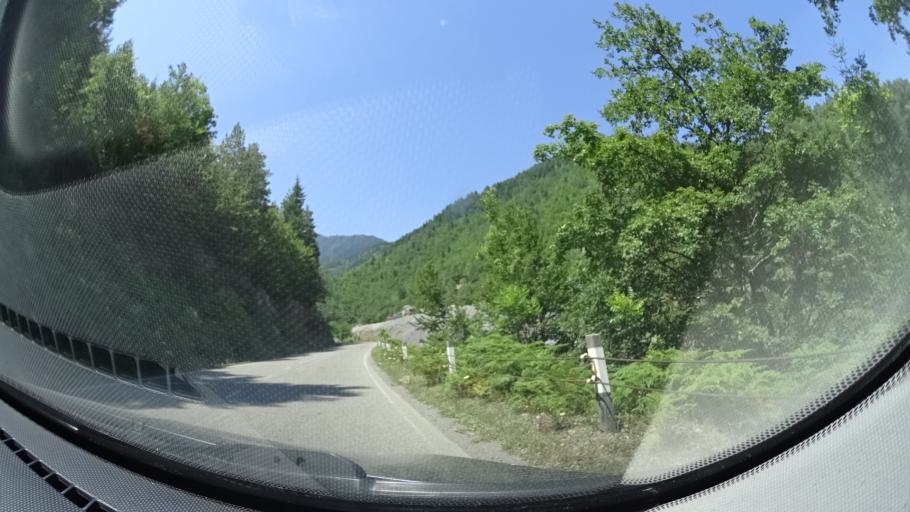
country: GE
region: Ajaria
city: Khulo
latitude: 41.6264
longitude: 42.2844
